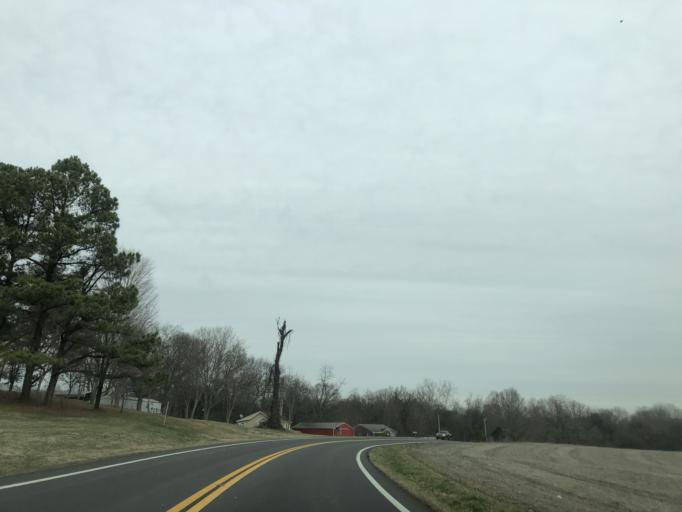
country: US
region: Tennessee
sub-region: Robertson County
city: Cross Plains
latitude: 36.4765
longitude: -86.7320
